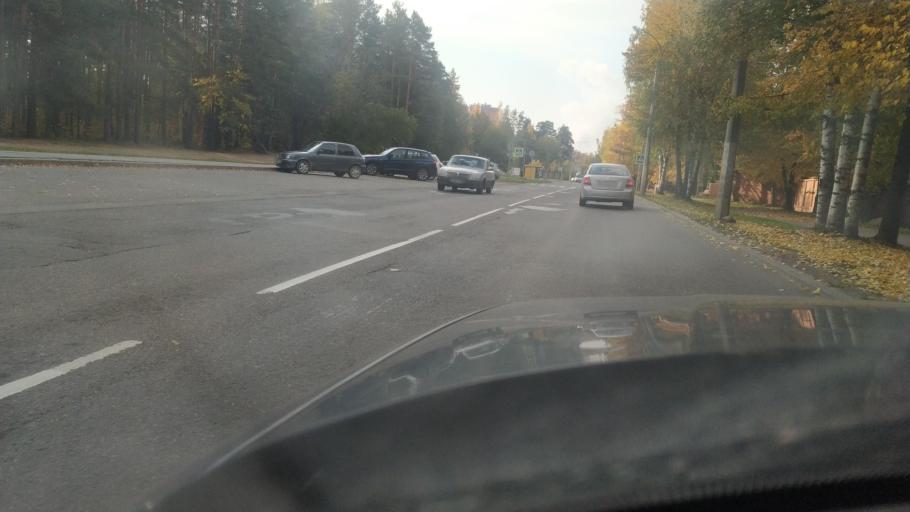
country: RU
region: Leningrad
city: Sosnovyy Bor
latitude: 59.8978
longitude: 29.1003
